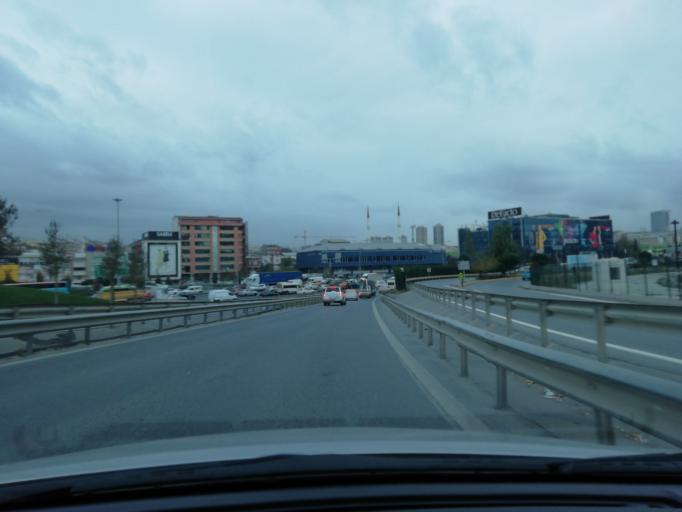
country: TR
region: Istanbul
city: Mahmutbey
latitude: 41.0463
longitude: 28.8091
